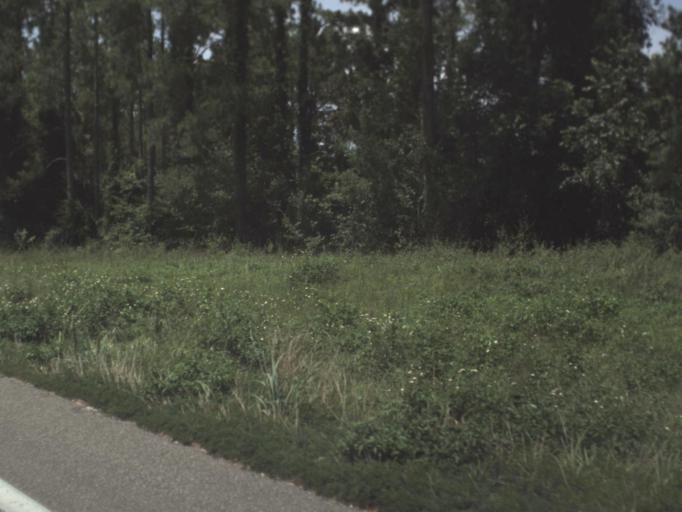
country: US
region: Florida
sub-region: Gilchrist County
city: Trenton
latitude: 29.6434
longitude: -82.8338
